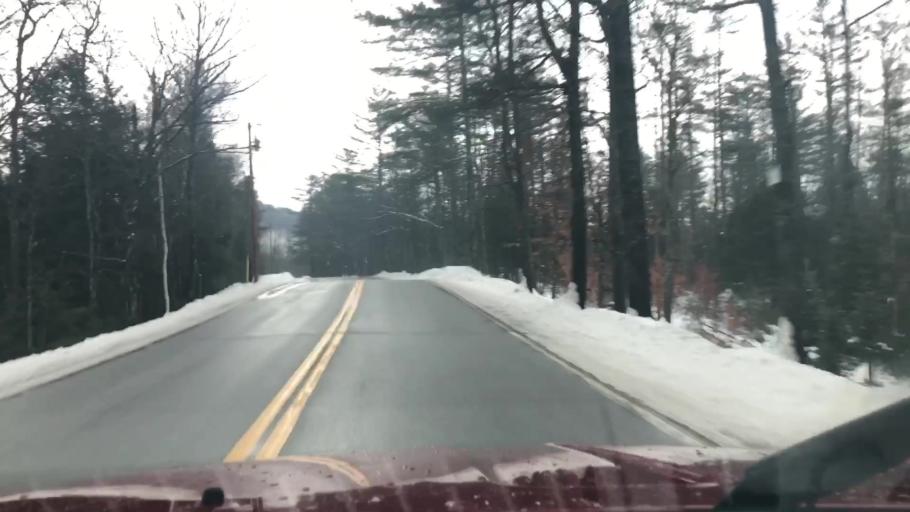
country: US
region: Maine
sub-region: Oxford County
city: West Paris
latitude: 44.4192
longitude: -70.6490
